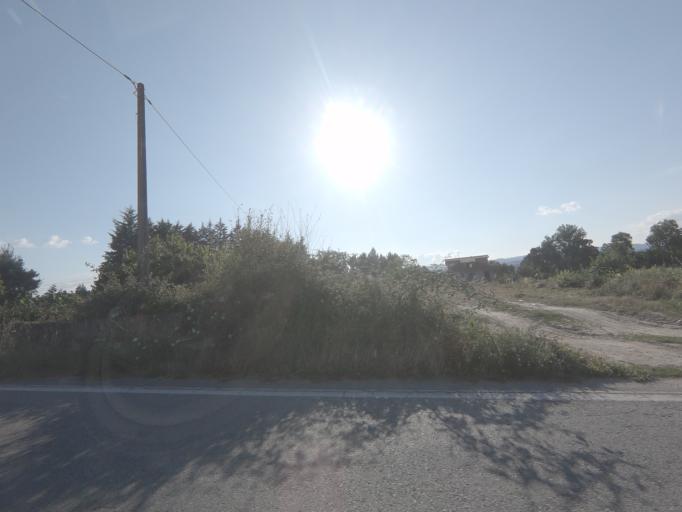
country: PT
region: Vila Real
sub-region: Chaves
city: Chaves
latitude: 41.8008
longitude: -7.4210
